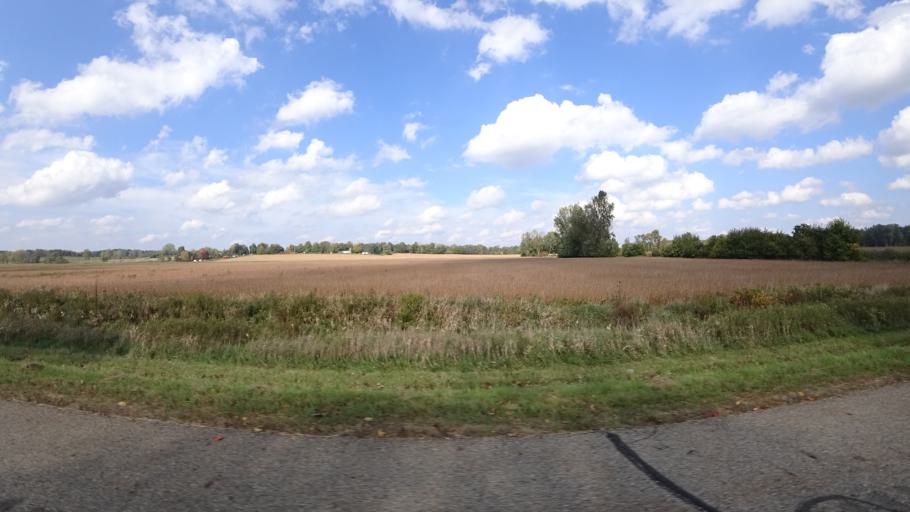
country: US
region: Michigan
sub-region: Branch County
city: Union City
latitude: 42.1059
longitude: -85.0211
